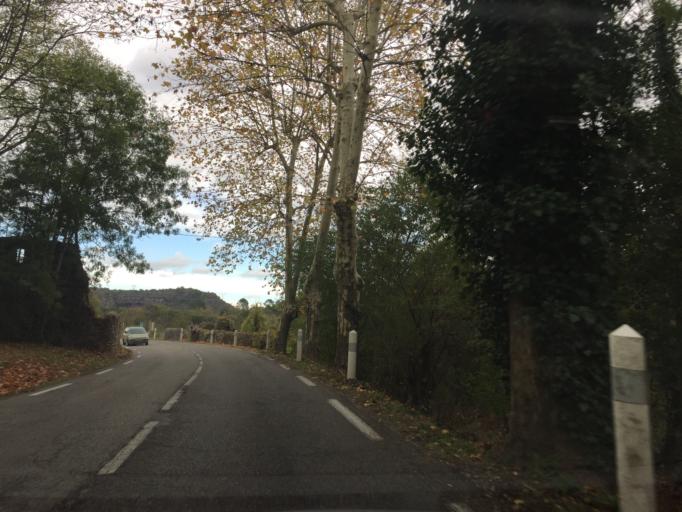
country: FR
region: Rhone-Alpes
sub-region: Departement de l'Ardeche
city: Les Vans
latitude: 44.4154
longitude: 4.1590
